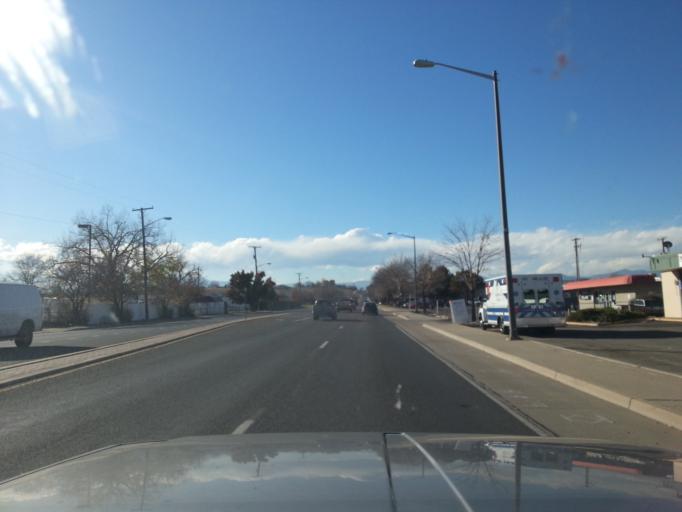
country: US
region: Colorado
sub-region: Larimer County
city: Loveland
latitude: 40.3784
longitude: -105.0747
